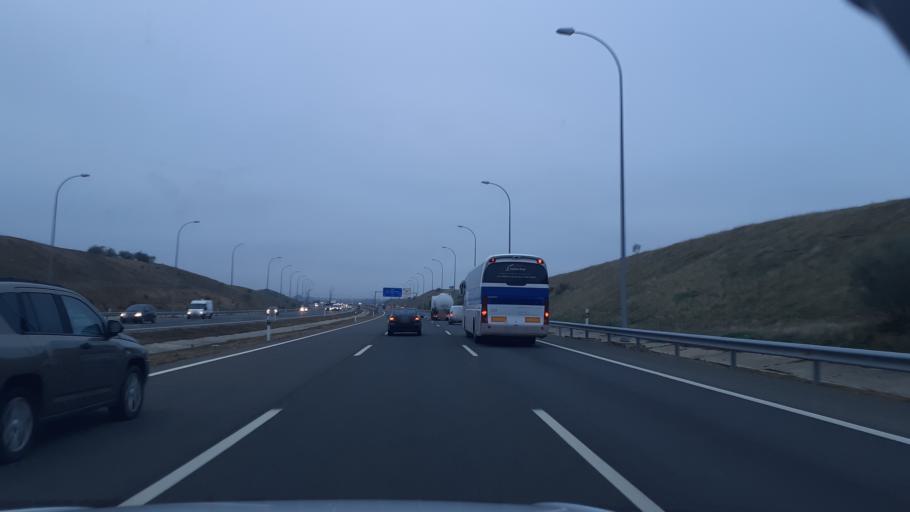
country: ES
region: Madrid
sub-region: Provincia de Madrid
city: Paracuellos de Jarama
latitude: 40.4888
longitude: -3.4966
